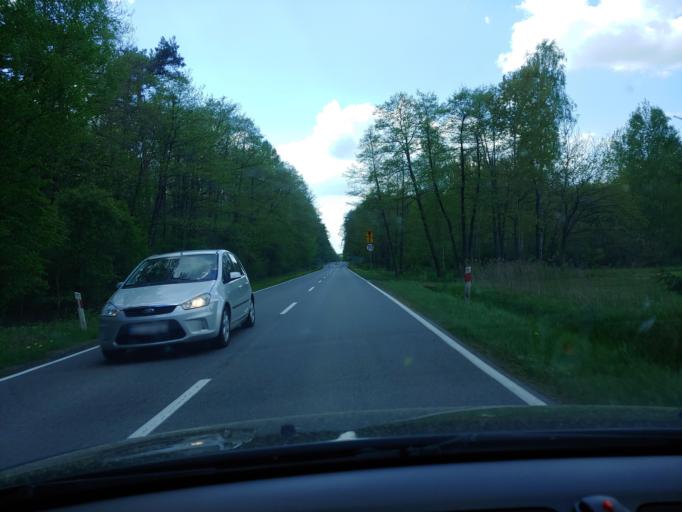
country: PL
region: Lesser Poland Voivodeship
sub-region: Powiat dabrowski
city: Radgoszcz
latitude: 50.1376
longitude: 21.1673
